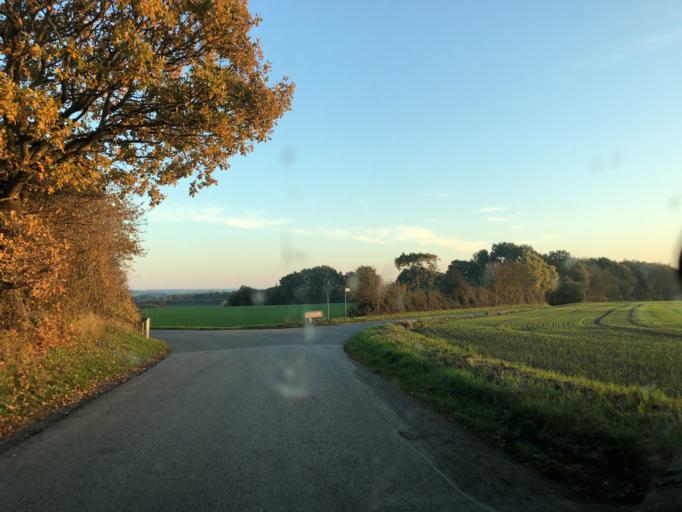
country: DK
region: South Denmark
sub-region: Vejle Kommune
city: Borkop
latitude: 55.6254
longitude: 9.6481
